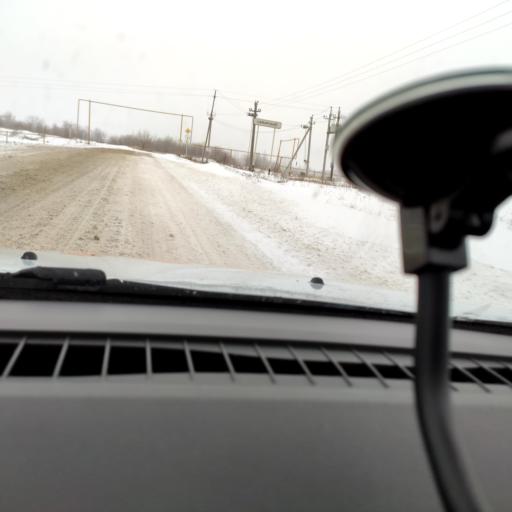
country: RU
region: Samara
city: Dubovyy Umet
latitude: 53.0412
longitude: 50.2411
